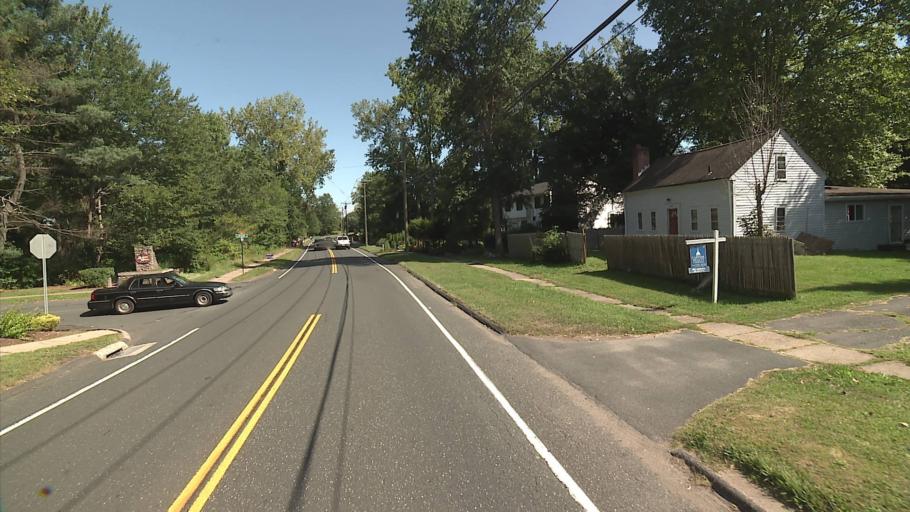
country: US
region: Connecticut
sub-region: Hartford County
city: Blue Hills
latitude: 41.8242
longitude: -72.7215
